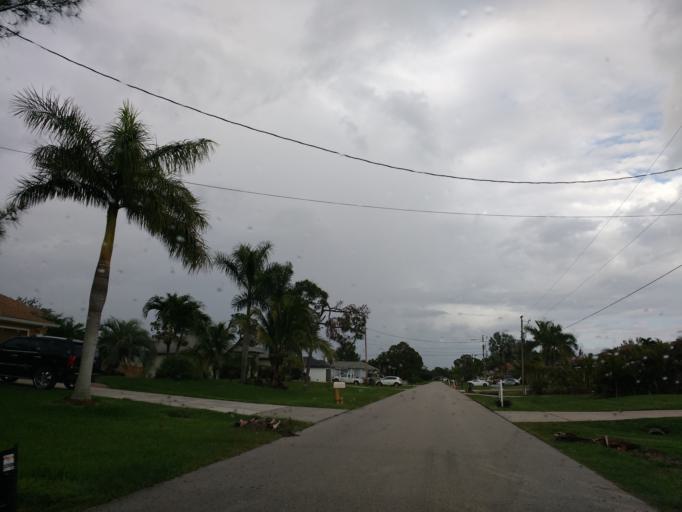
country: US
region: Florida
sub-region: Lee County
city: Cape Coral
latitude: 26.6108
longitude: -82.0209
